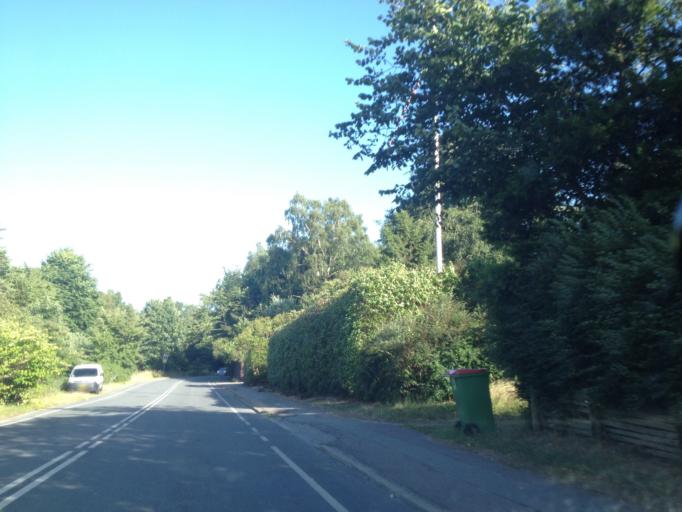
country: DK
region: Capital Region
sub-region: Gribskov Kommune
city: Helsinge
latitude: 56.0542
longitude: 12.1030
